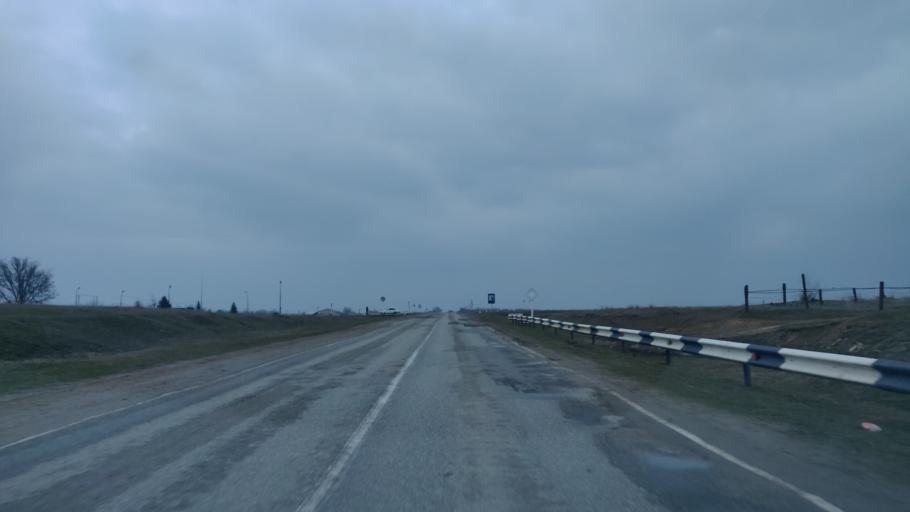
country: RU
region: Stavropol'skiy
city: Letnyaya Stavka
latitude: 45.3761
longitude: 43.3173
